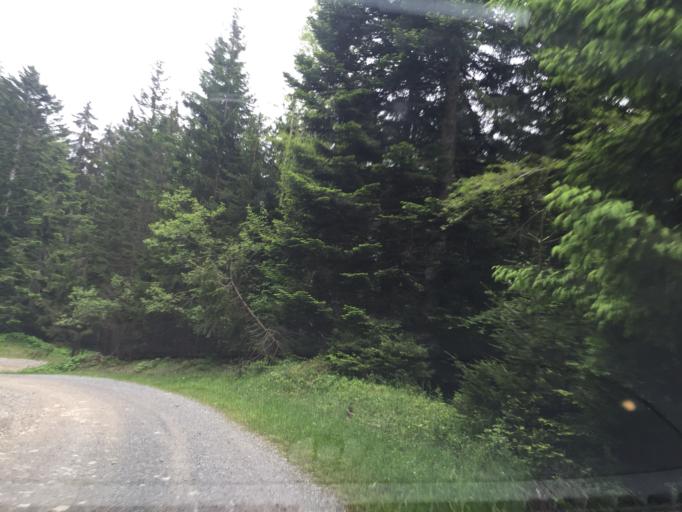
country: FR
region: Rhone-Alpes
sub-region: Departement de la Savoie
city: La Rochette
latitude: 45.4393
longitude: 6.1740
